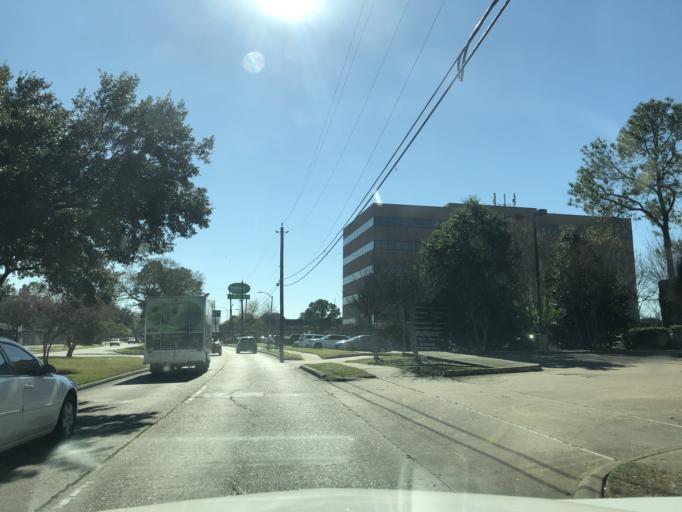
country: US
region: Texas
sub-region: Harris County
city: Bellaire
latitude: 29.6766
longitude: -95.4939
